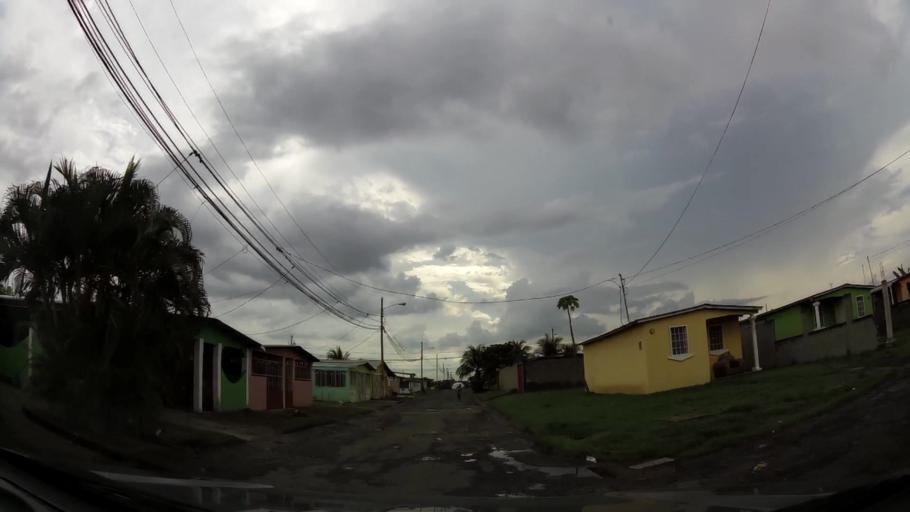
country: PA
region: Panama
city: Cabra Numero Uno
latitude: 9.0929
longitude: -79.3481
